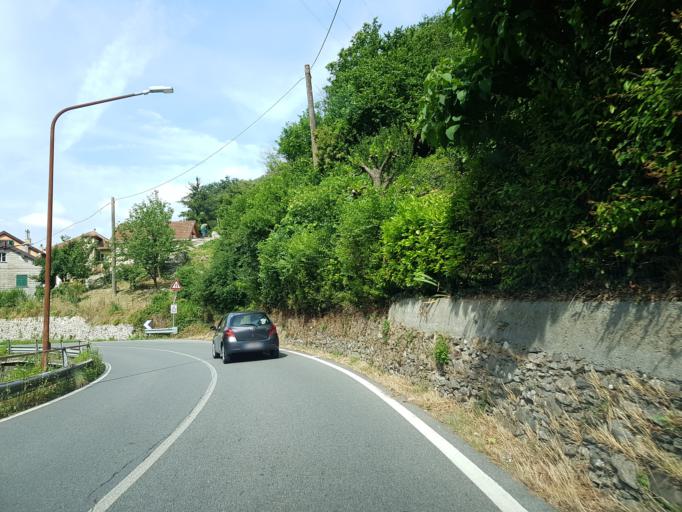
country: IT
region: Liguria
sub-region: Provincia di Genova
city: Manesseno
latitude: 44.4810
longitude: 8.9427
